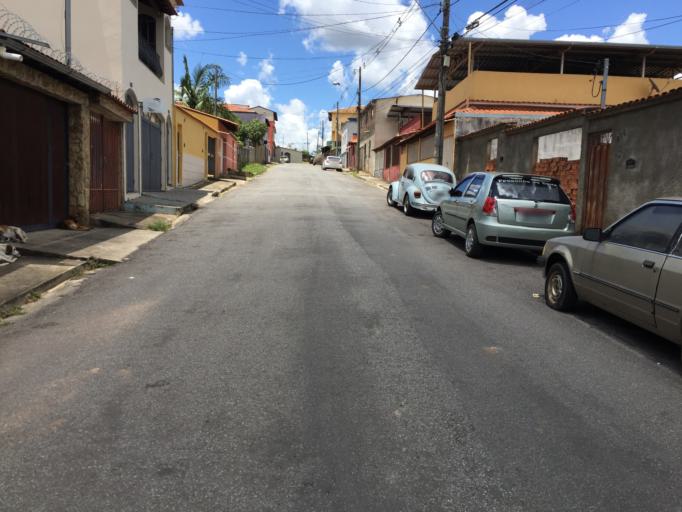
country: BR
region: Minas Gerais
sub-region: Sao Joao Del Rei
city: Sao Joao del Rei
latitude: -21.1440
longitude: -44.2670
